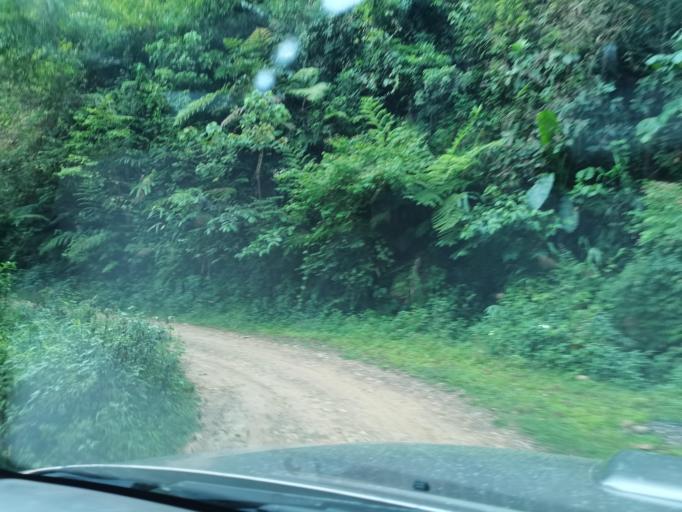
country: LA
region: Phongsali
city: Phongsali
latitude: 21.6512
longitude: 102.1530
